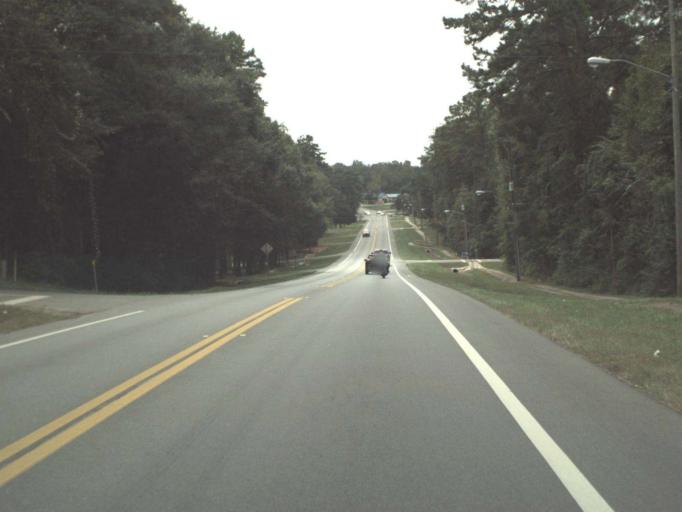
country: US
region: Florida
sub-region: Jackson County
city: Marianna
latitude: 30.7880
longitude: -85.2255
